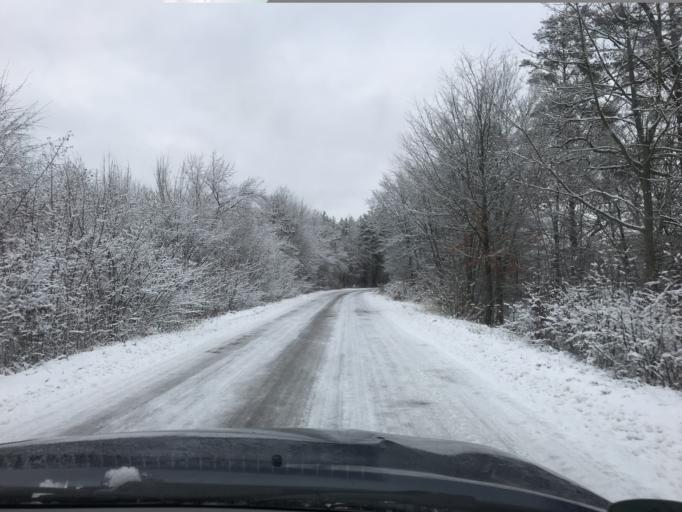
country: PL
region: Pomeranian Voivodeship
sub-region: Powiat bytowski
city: Parchowo
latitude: 54.2465
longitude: 17.5778
